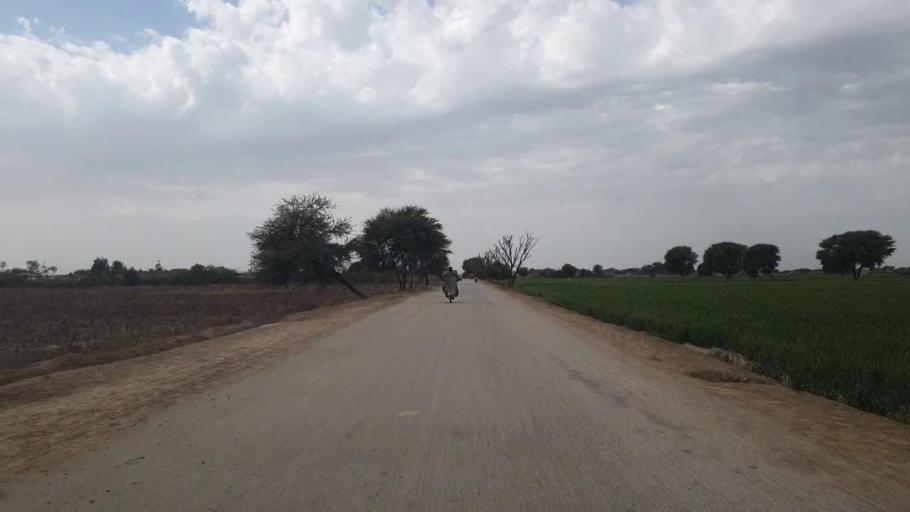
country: PK
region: Sindh
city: Hala
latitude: 25.9359
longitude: 68.4169
